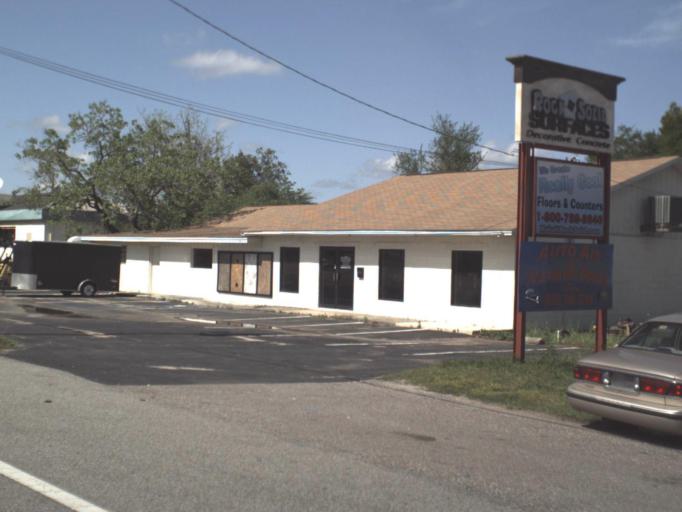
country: US
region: Florida
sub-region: Escambia County
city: Cantonment
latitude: 30.6067
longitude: -87.3171
